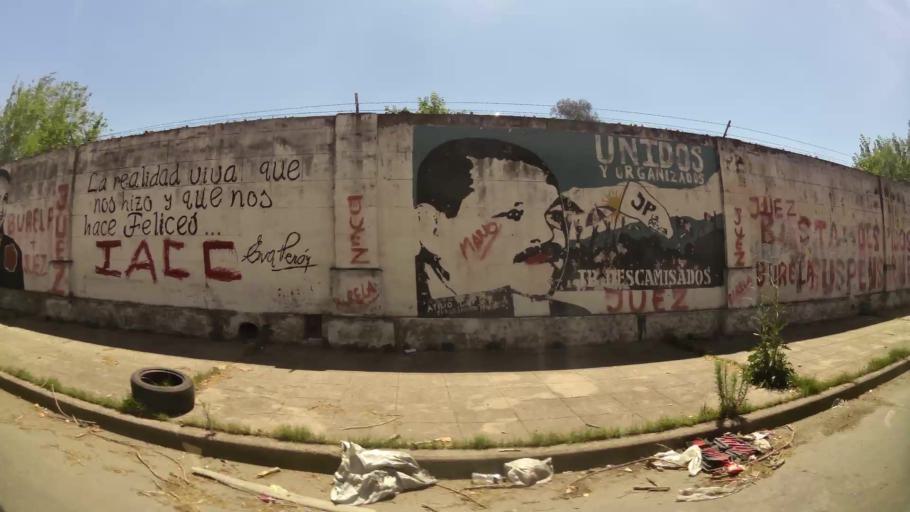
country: AR
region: Cordoba
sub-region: Departamento de Capital
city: Cordoba
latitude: -31.3892
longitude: -64.1924
